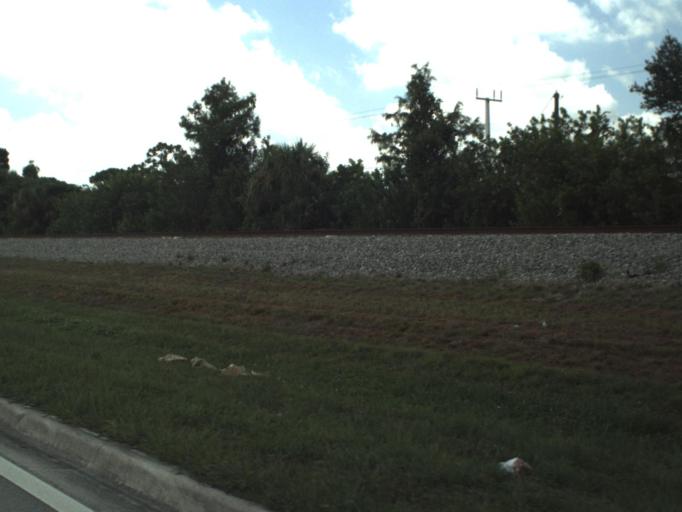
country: US
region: Florida
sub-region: Palm Beach County
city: North Palm Beach
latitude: 26.8253
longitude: -80.0890
